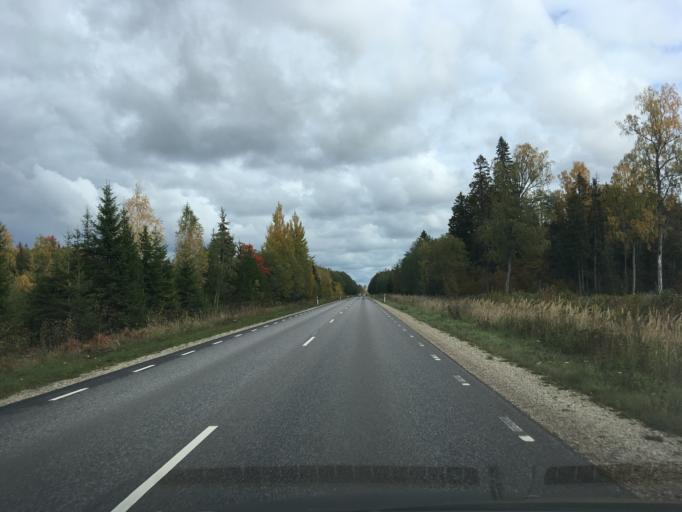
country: EE
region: Harju
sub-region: Anija vald
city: Kehra
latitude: 59.2374
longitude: 25.2900
